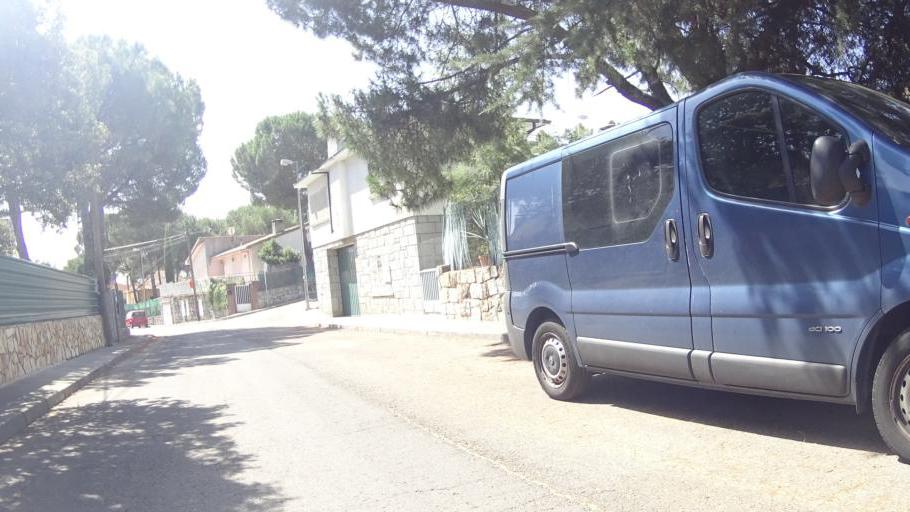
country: ES
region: Madrid
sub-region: Provincia de Madrid
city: Colmenarejo
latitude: 40.5598
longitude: -4.0099
